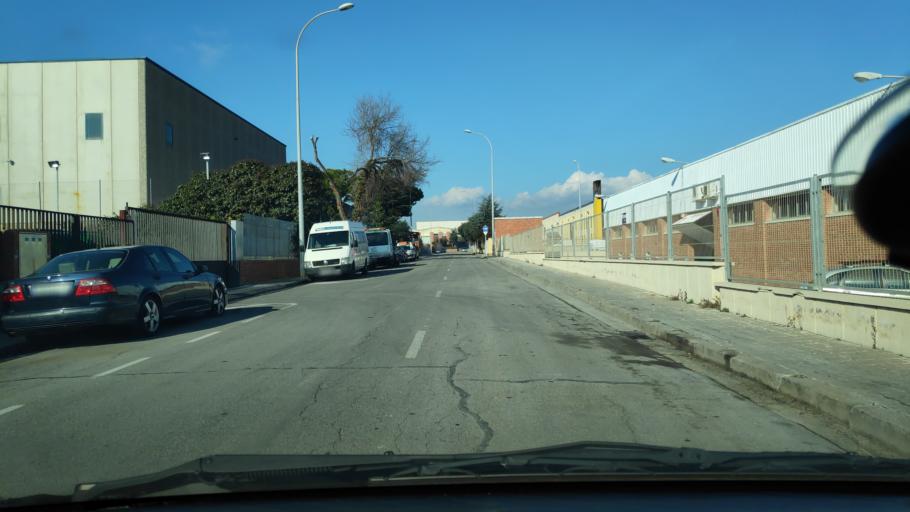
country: ES
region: Catalonia
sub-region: Provincia de Barcelona
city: Sant Quirze del Valles
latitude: 41.5214
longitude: 2.0946
